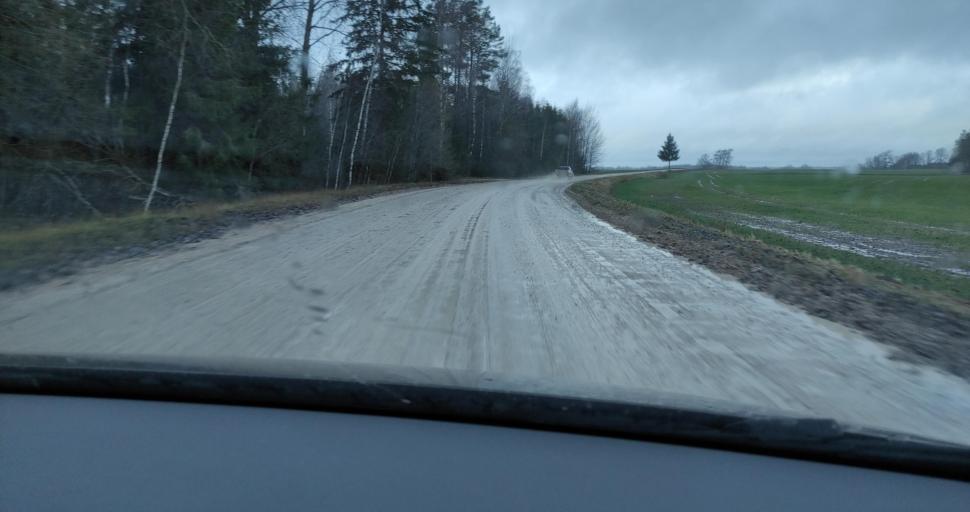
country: LV
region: Skrunda
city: Skrunda
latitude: 56.6948
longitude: 22.2175
